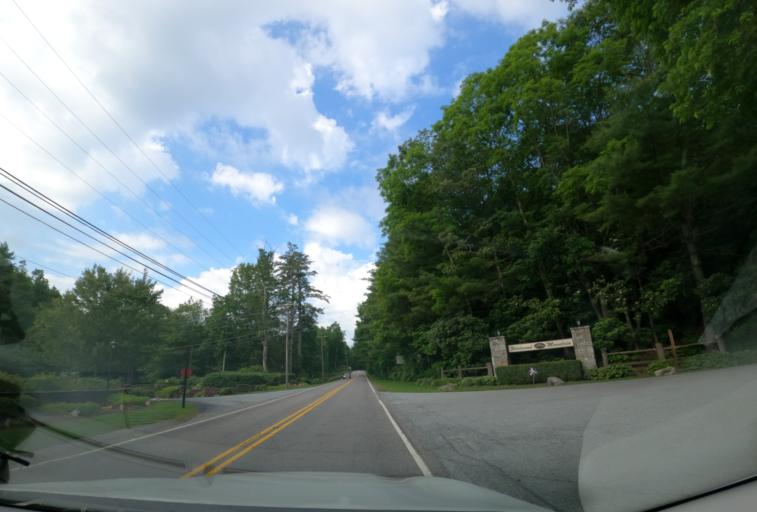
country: US
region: North Carolina
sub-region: Jackson County
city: Cullowhee
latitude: 35.0913
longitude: -83.1582
